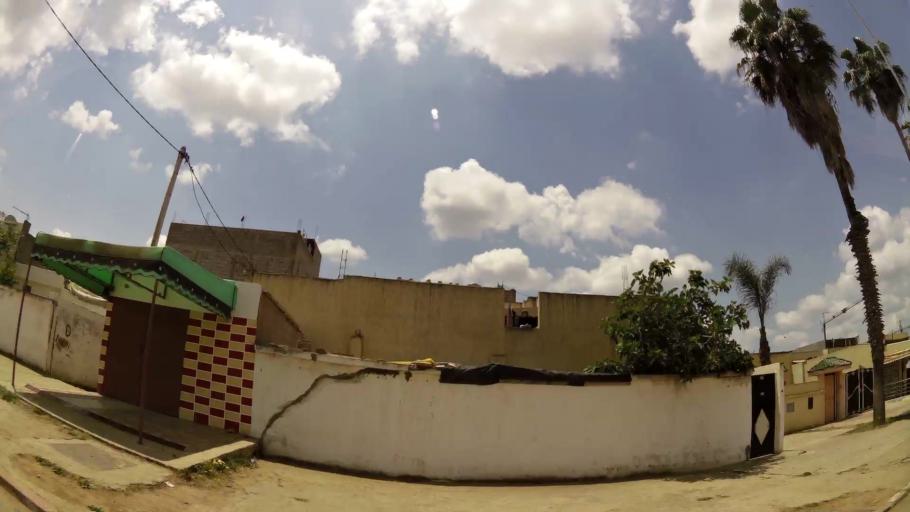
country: MA
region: Rabat-Sale-Zemmour-Zaer
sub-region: Khemisset
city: Tiflet
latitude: 34.0053
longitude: -6.5288
